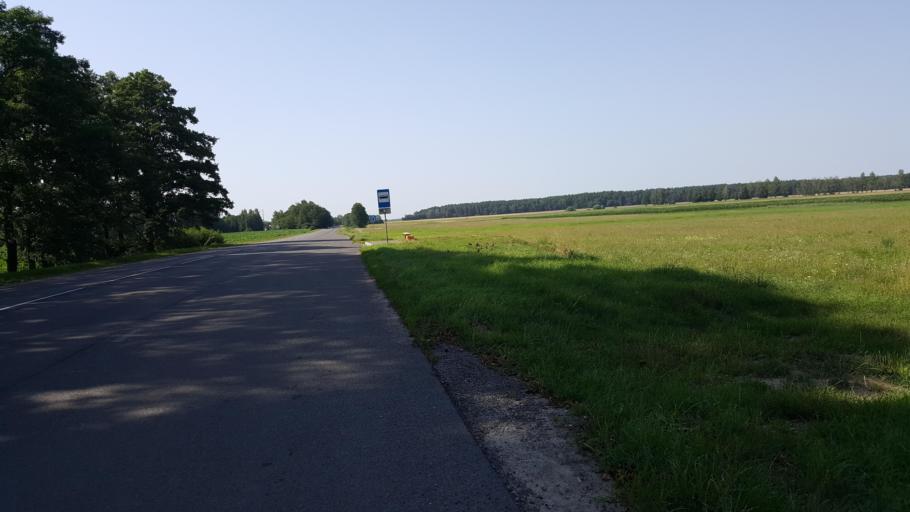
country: BY
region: Brest
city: Zhabinka
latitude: 52.2297
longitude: 23.9855
